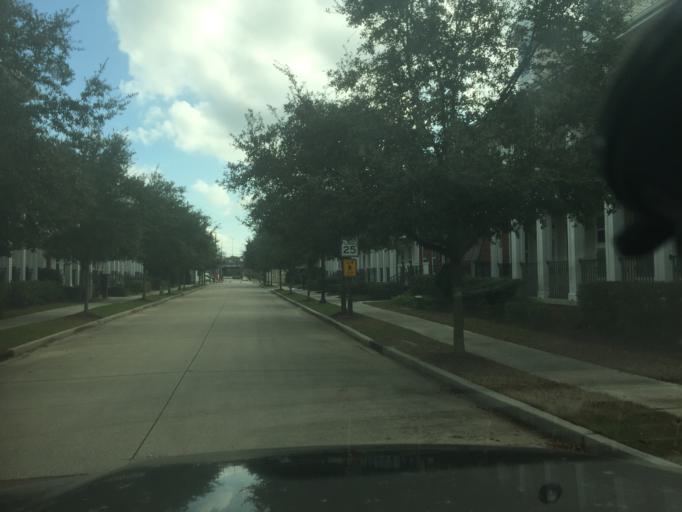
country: US
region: Louisiana
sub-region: Orleans Parish
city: New Orleans
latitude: 29.9949
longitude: -90.0758
